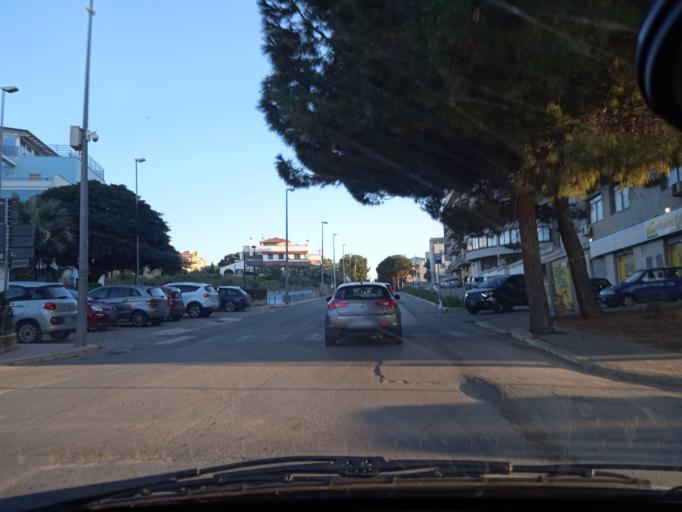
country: IT
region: Sicily
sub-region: Palermo
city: Bagheria
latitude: 38.0873
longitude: 13.5008
